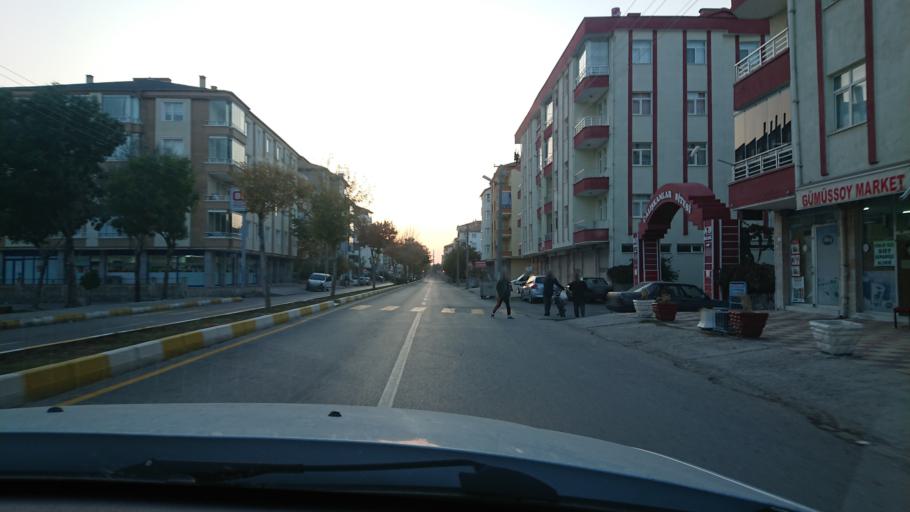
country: TR
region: Aksaray
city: Aksaray
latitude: 38.3632
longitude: 34.0330
